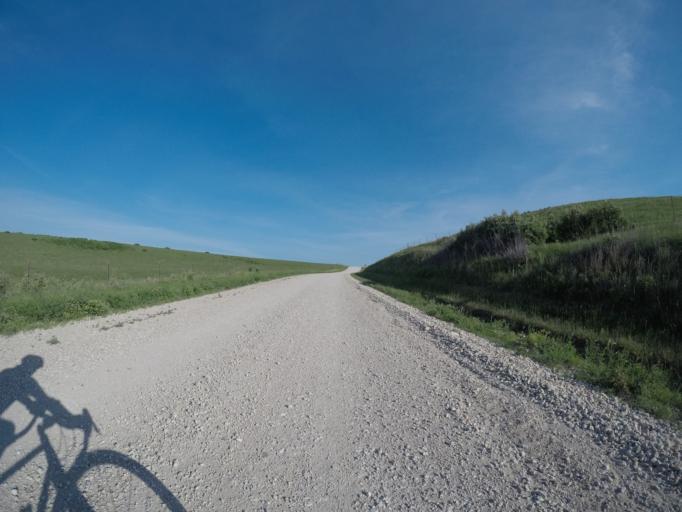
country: US
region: Kansas
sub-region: Riley County
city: Manhattan
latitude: 39.0412
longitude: -96.4917
